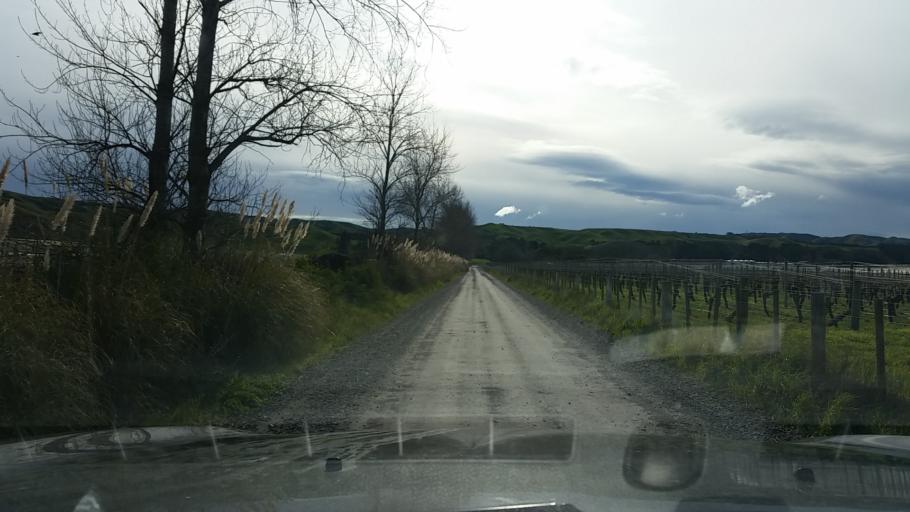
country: NZ
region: Marlborough
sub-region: Marlborough District
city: Blenheim
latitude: -41.6255
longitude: 174.1002
